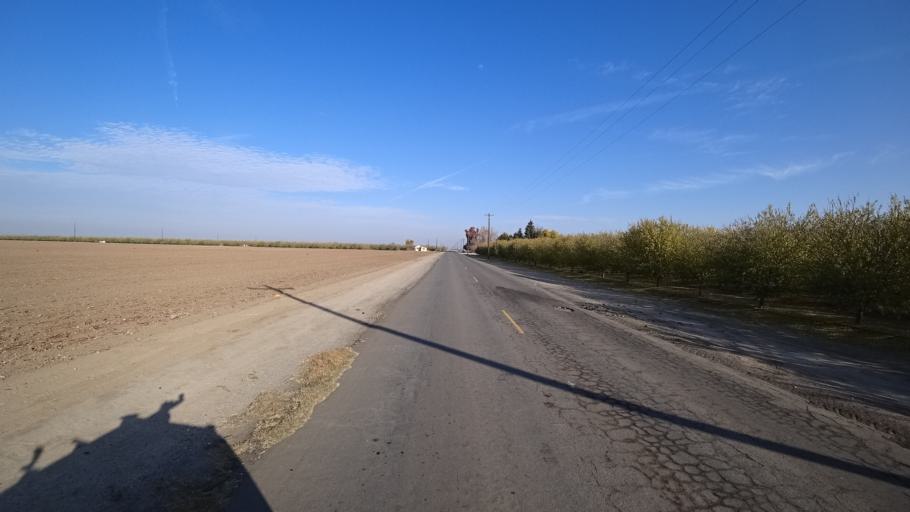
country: US
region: California
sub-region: Kern County
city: Greenfield
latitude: 35.2498
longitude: -119.0922
